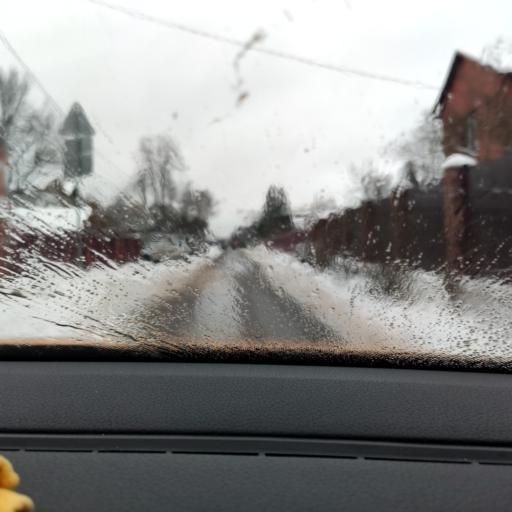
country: RU
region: Moscow
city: Strogino
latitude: 55.7865
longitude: 37.4010
